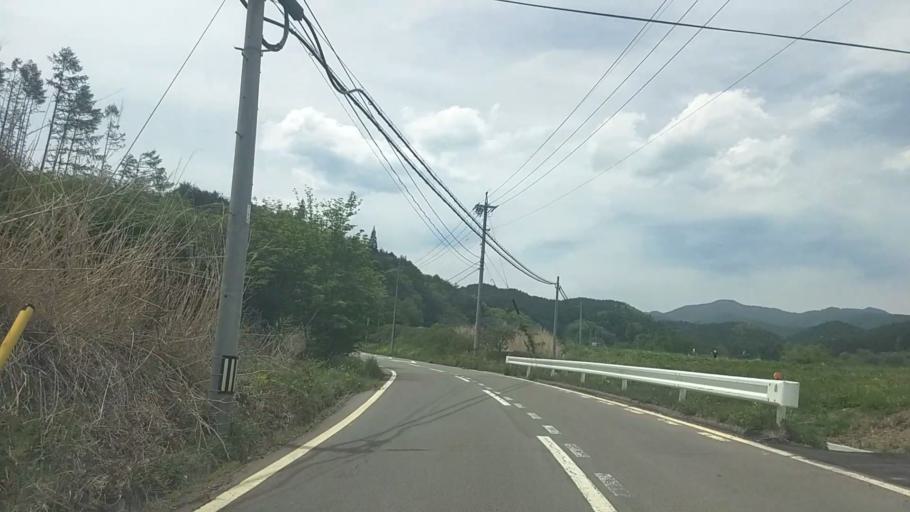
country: JP
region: Nagano
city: Saku
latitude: 36.1075
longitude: 138.4319
